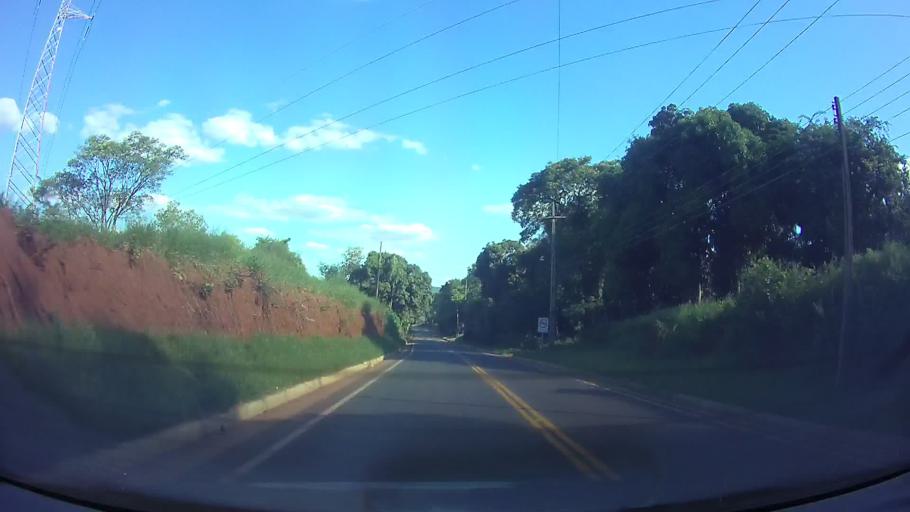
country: PY
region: Cordillera
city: Caacupe
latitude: -25.3700
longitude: -57.1415
